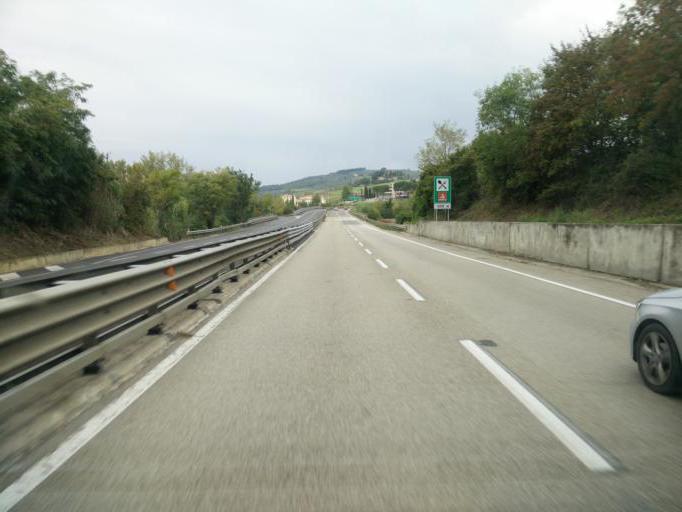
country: IT
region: Tuscany
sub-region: Provincia di Siena
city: Poggibonsi
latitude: 43.4835
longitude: 11.1512
